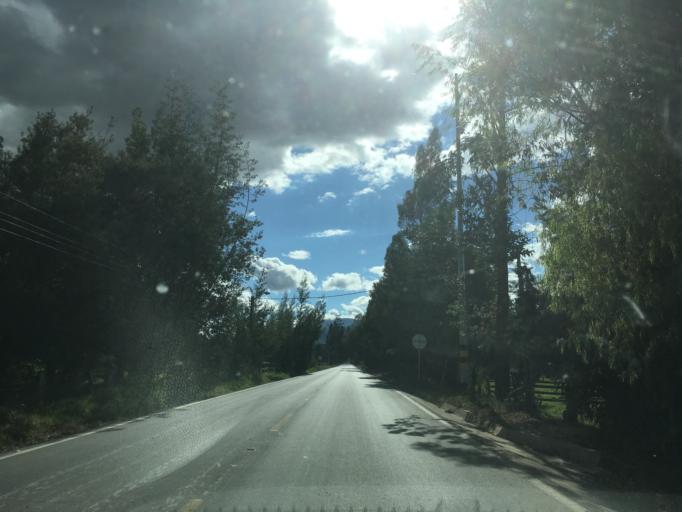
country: CO
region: Boyaca
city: Firavitoba
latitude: 5.6421
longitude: -72.9913
